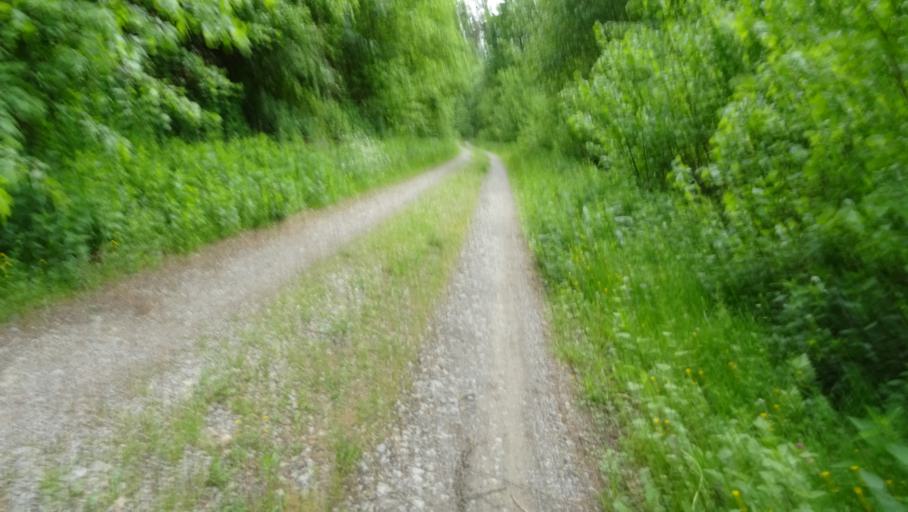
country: DE
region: Baden-Wuerttemberg
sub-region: Karlsruhe Region
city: Neckargerach
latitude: 49.4161
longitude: 9.0959
